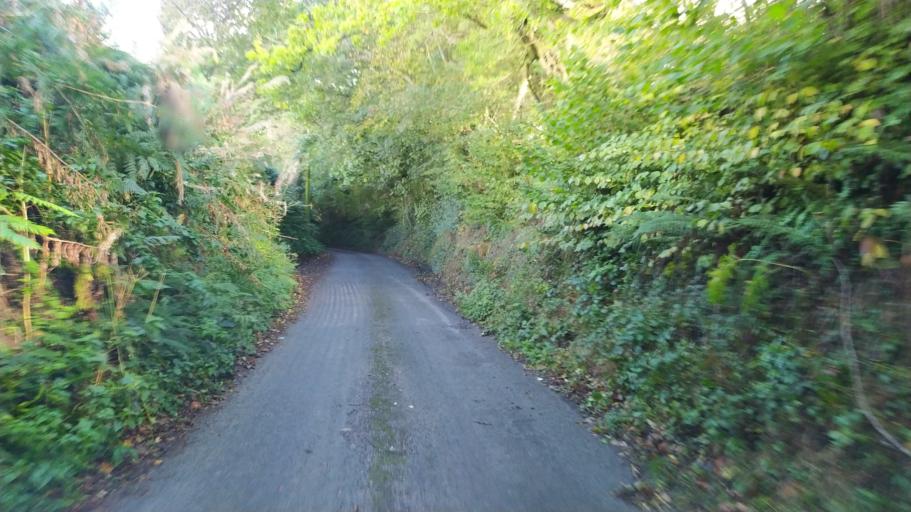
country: GB
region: England
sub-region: Wiltshire
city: Hindon
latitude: 51.0351
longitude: -2.1336
